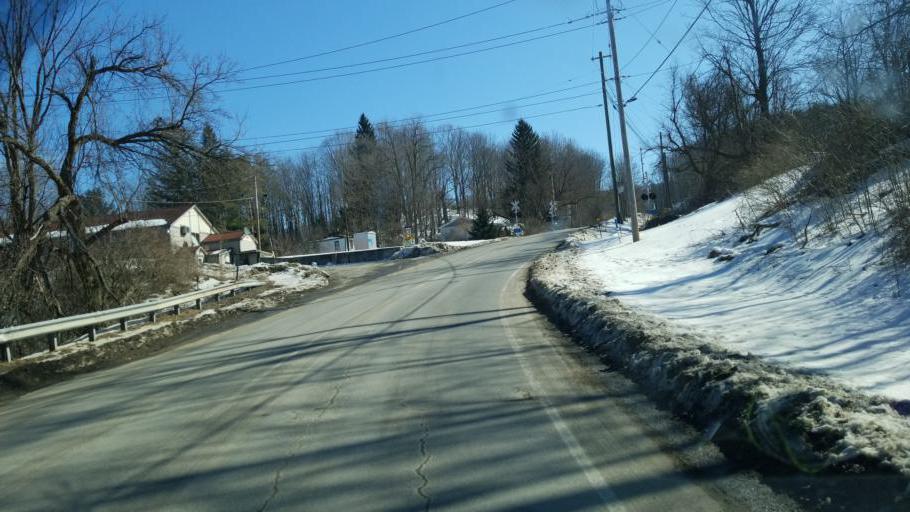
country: US
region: New York
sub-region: Allegany County
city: Alfred
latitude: 42.2676
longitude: -77.7579
